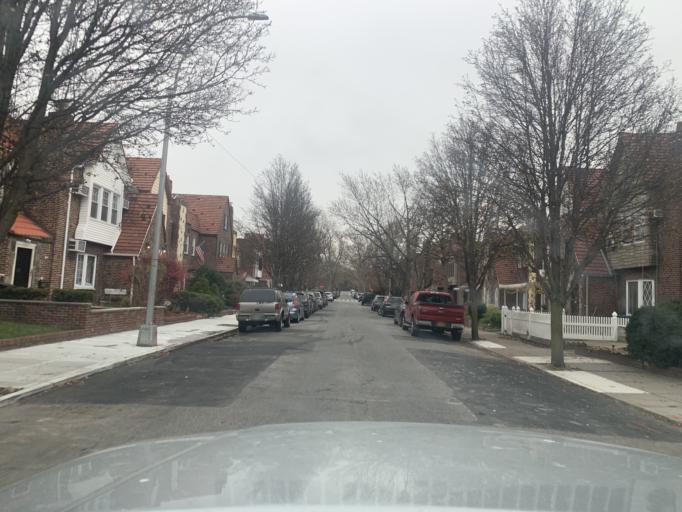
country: US
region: New York
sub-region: Queens County
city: Borough of Queens
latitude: 40.7214
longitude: -73.8696
